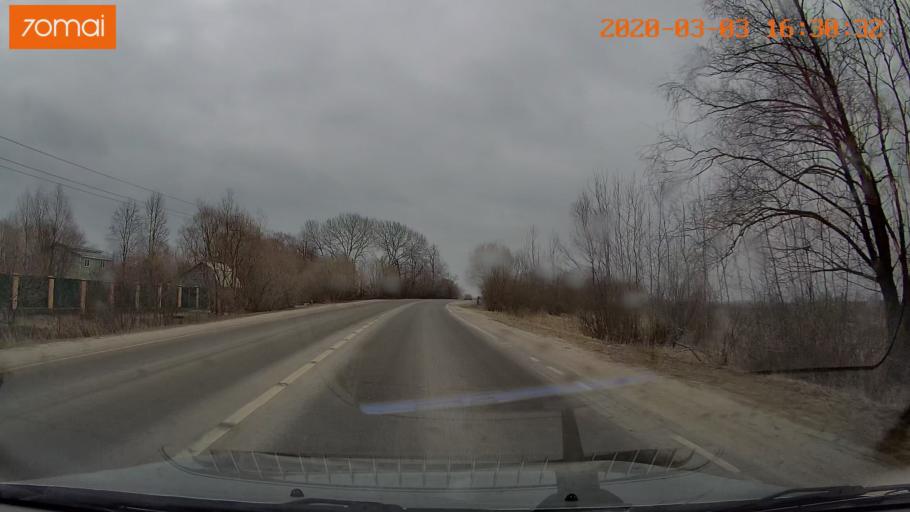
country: RU
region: Moskovskaya
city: Konobeyevo
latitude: 55.4325
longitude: 38.7125
